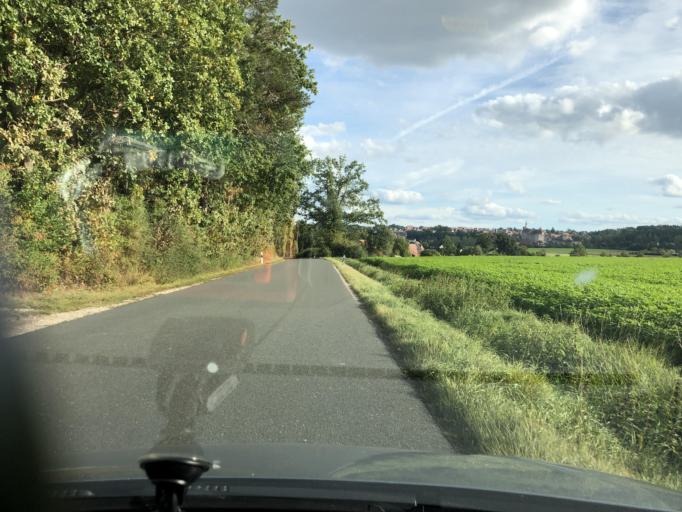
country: DE
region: Bavaria
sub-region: Regierungsbezirk Mittelfranken
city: Cadolzburg
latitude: 49.4721
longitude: 10.8407
